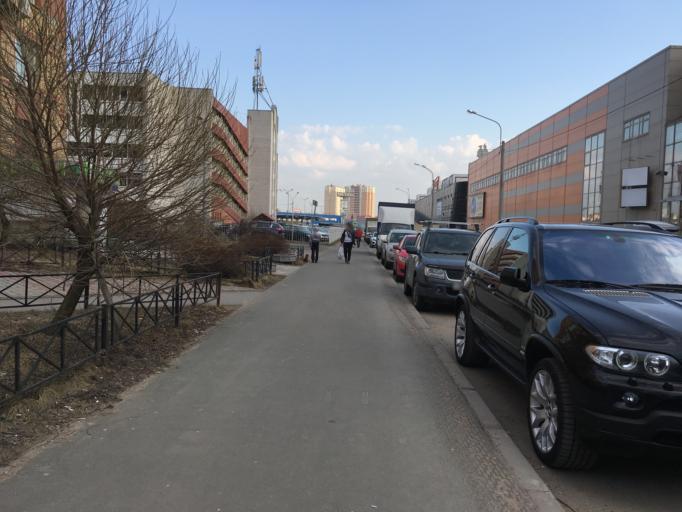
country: RU
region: St.-Petersburg
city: Komendantsky aerodrom
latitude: 60.0047
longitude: 30.2639
